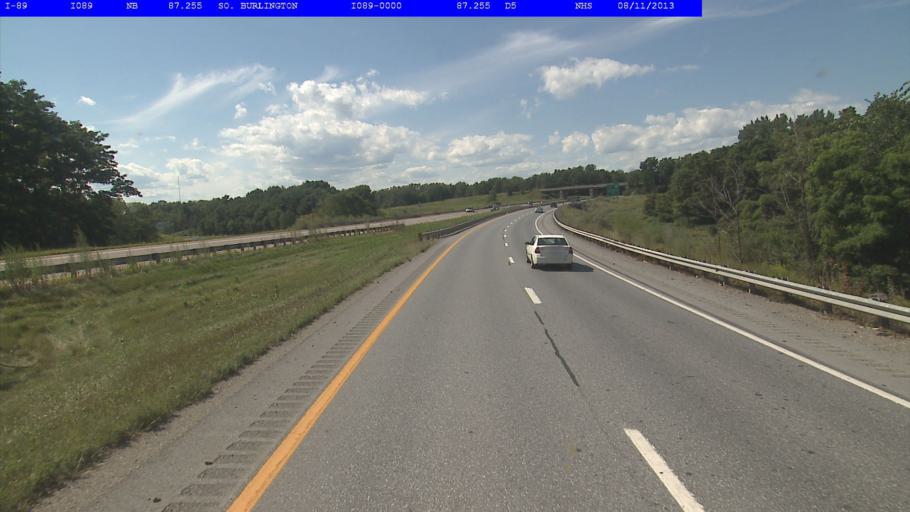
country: US
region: Vermont
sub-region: Chittenden County
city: South Burlington
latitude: 44.4502
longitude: -73.1791
